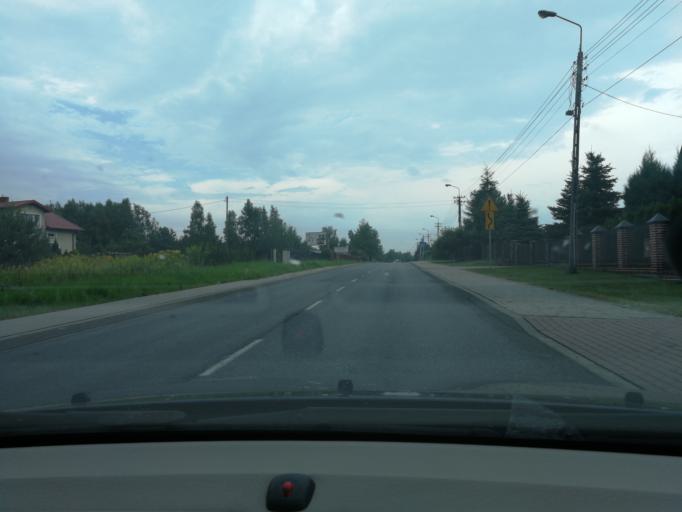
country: PL
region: Masovian Voivodeship
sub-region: Powiat zyrardowski
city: Radziejowice
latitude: 52.0072
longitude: 20.5573
